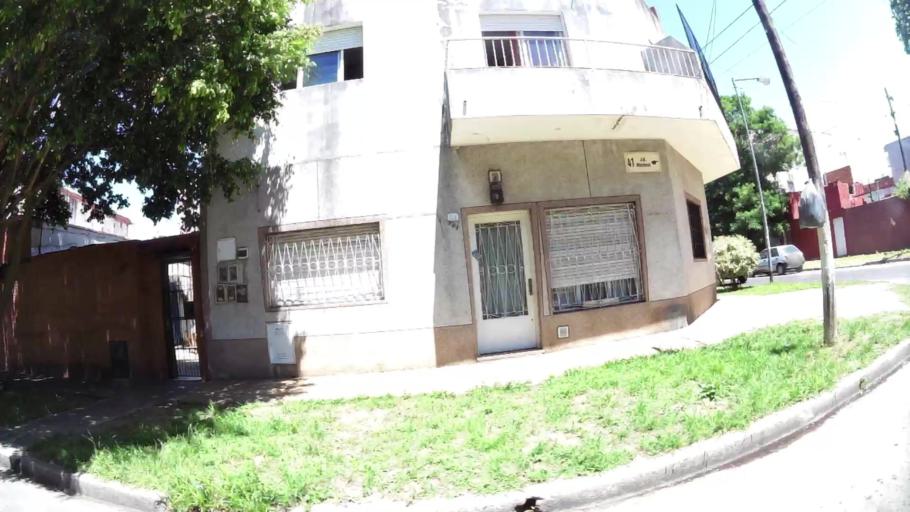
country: AR
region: Buenos Aires
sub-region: Partido de General San Martin
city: General San Martin
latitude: -34.5684
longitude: -58.5194
